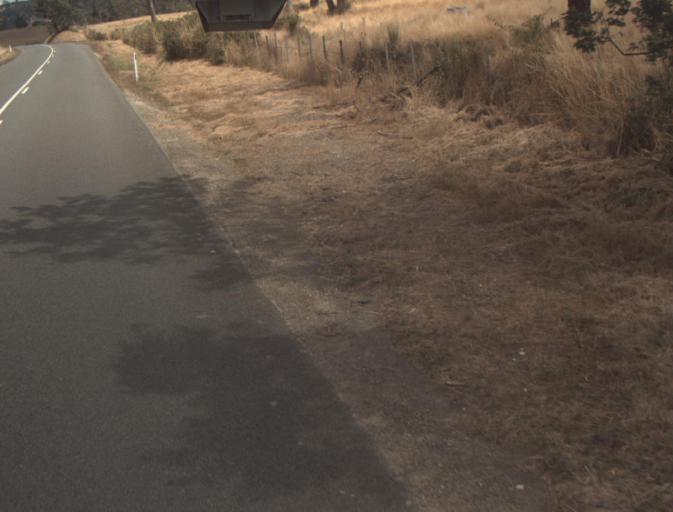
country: AU
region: Tasmania
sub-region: Launceston
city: Mayfield
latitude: -41.2186
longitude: 147.1216
